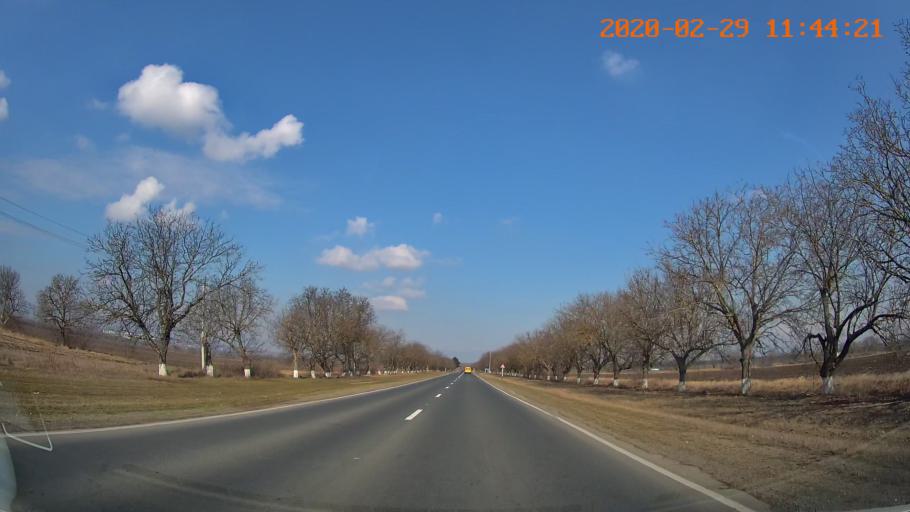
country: MD
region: Rezina
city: Saharna
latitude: 47.7101
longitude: 29.0009
